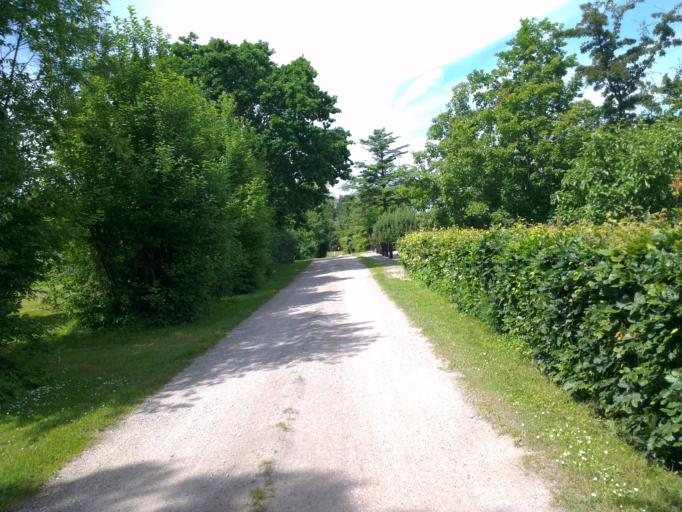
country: DK
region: Capital Region
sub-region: Frederikssund Kommune
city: Jaegerspris
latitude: 55.8182
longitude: 11.9447
